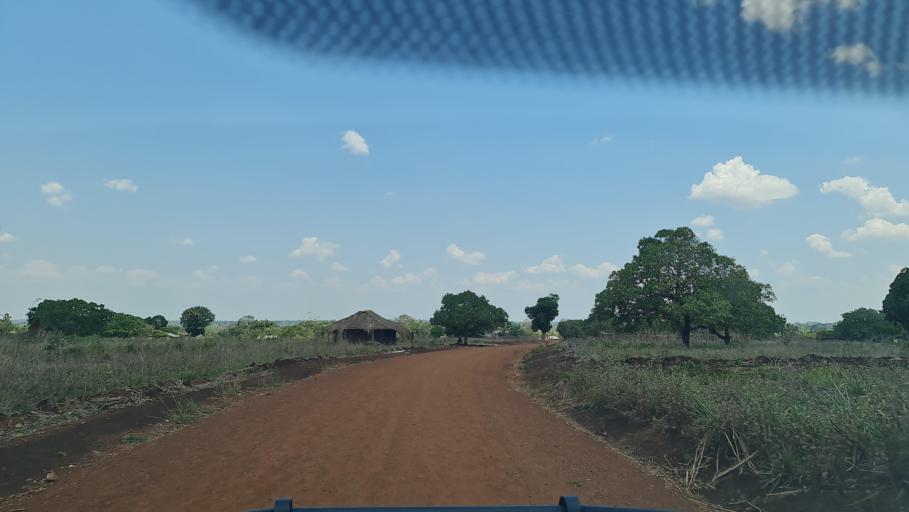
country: MZ
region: Nampula
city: Nacala
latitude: -14.8152
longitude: 40.0725
